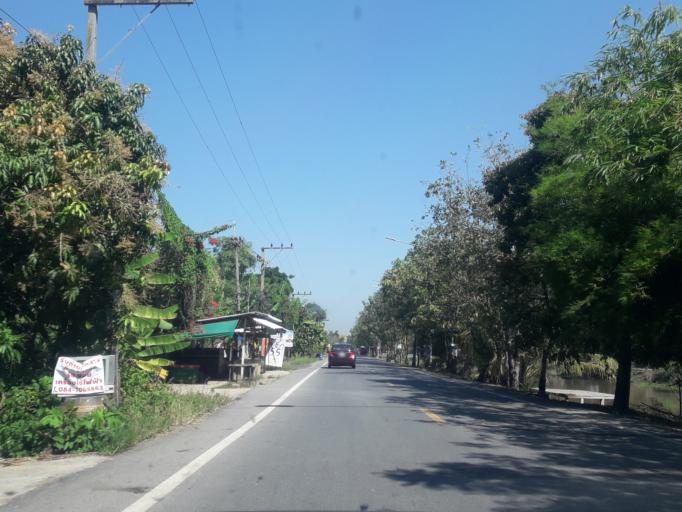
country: TH
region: Pathum Thani
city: Nong Suea
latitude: 14.1760
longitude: 100.8458
